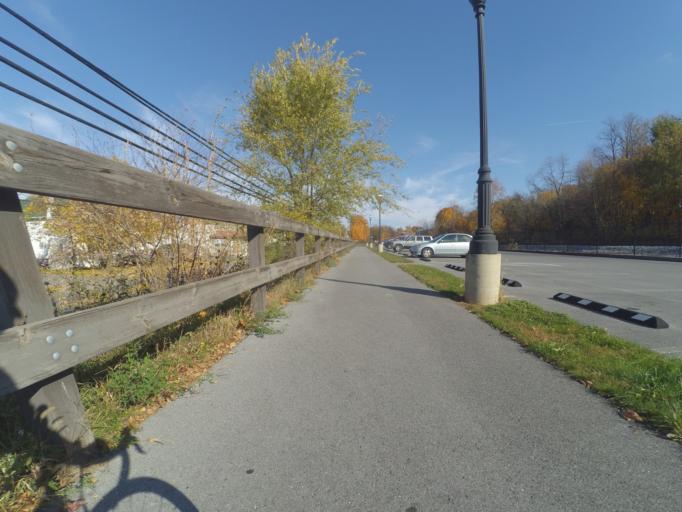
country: US
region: Pennsylvania
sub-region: Lycoming County
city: Jersey Shore
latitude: 41.2017
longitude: -77.2798
